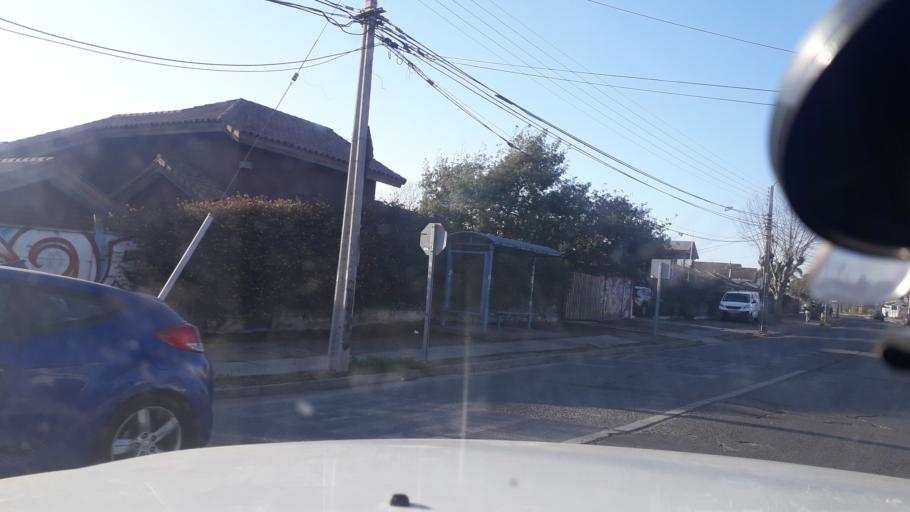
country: CL
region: Valparaiso
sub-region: Provincia de Valparaiso
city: Vina del Mar
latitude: -32.9294
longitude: -71.5186
